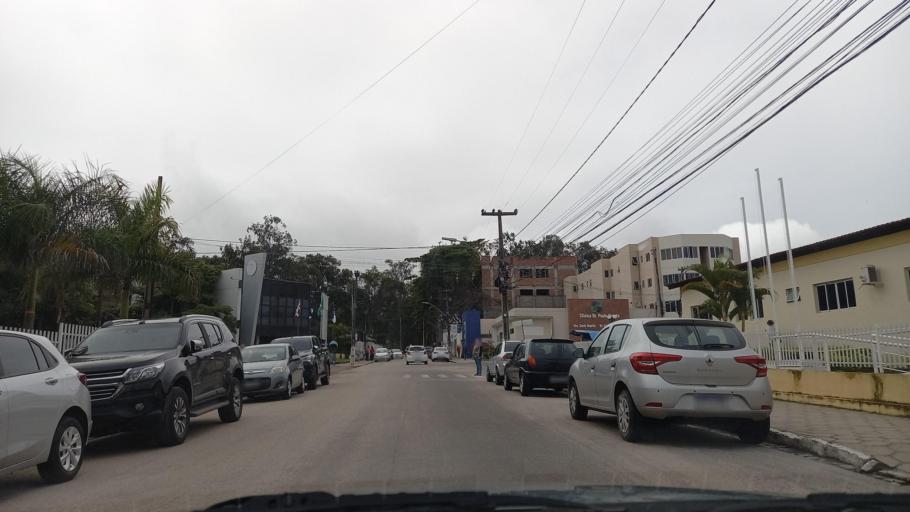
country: BR
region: Pernambuco
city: Garanhuns
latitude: -8.8854
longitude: -36.4872
